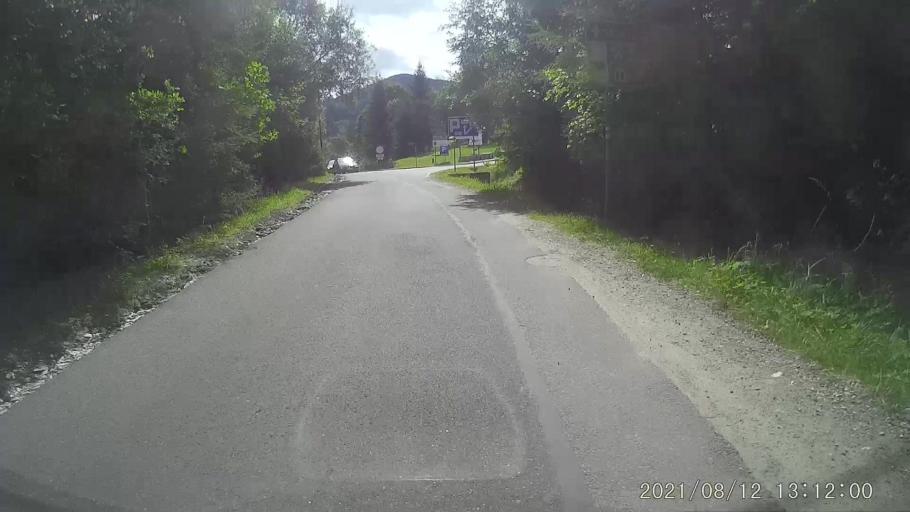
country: PL
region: Lower Silesian Voivodeship
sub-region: Powiat klodzki
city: Stronie Slaskie
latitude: 50.2447
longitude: 16.8529
